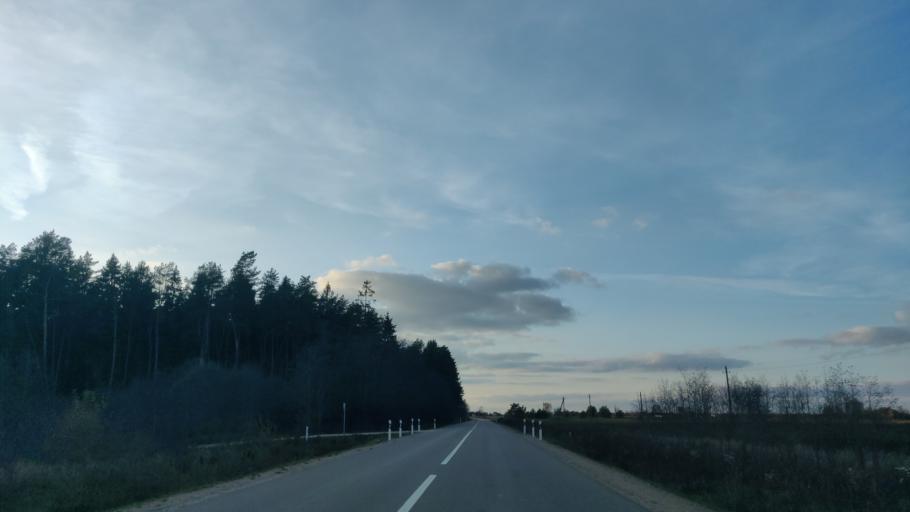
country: LT
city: Lentvaris
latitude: 54.5982
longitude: 25.0268
